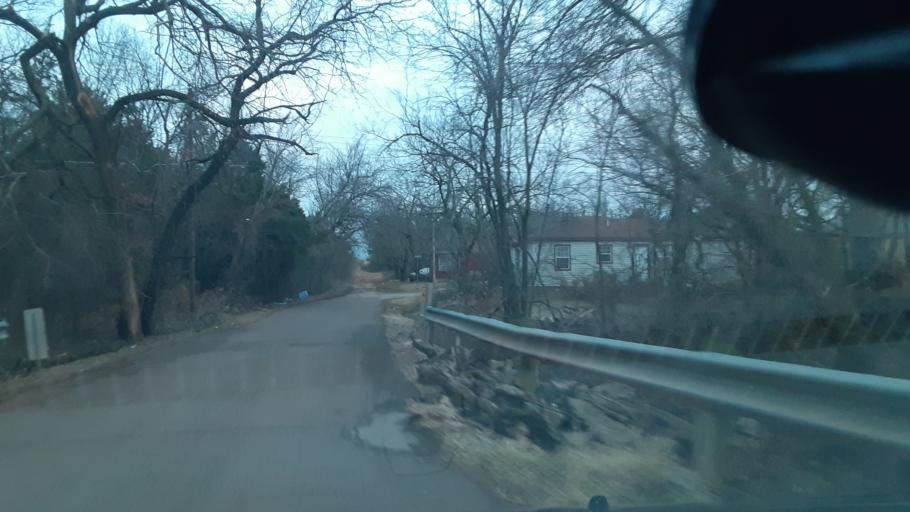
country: US
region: Oklahoma
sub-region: Logan County
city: Guthrie
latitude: 35.8708
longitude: -97.4123
